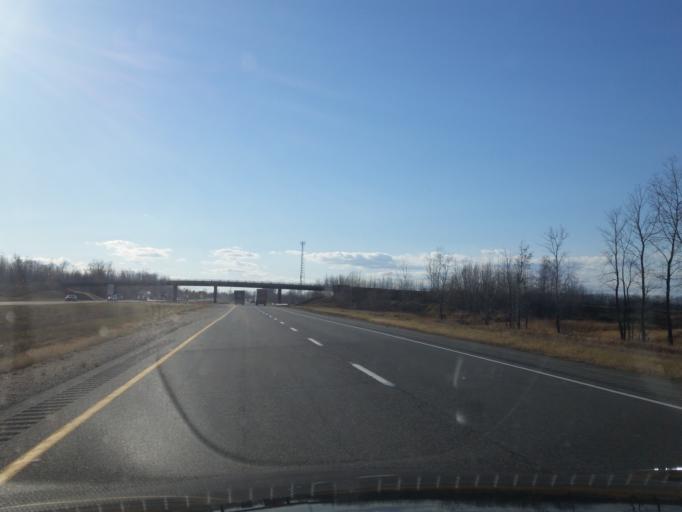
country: CA
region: Quebec
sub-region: Mauricie
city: Louiseville
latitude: 46.2339
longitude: -72.9166
